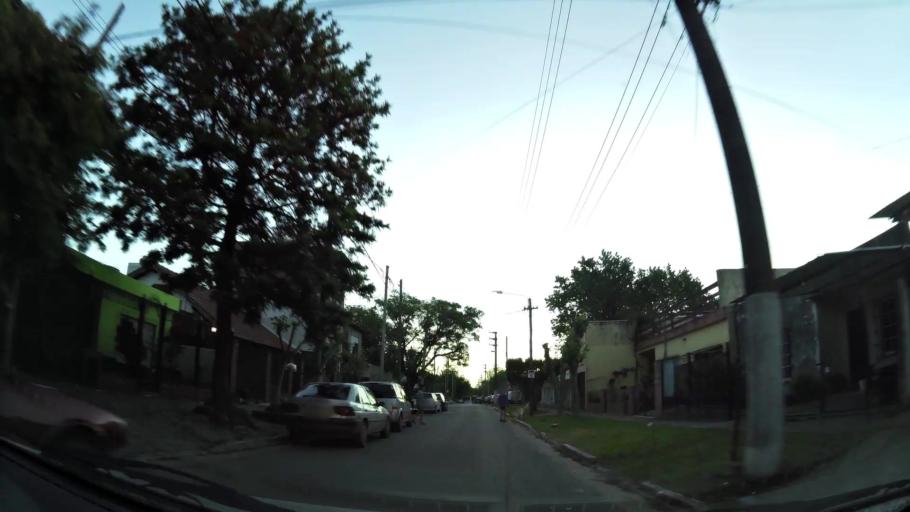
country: AR
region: Buenos Aires
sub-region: Partido de Quilmes
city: Quilmes
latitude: -34.7708
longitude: -58.2026
